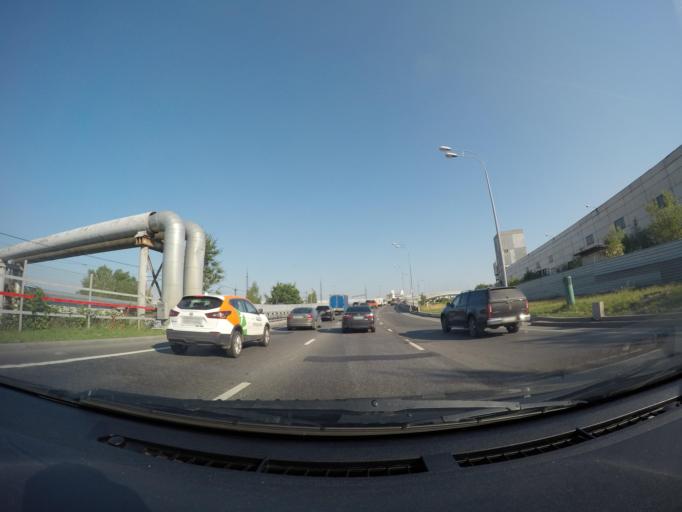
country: RU
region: Moscow
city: Ryazanskiy
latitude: 55.7490
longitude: 37.7483
